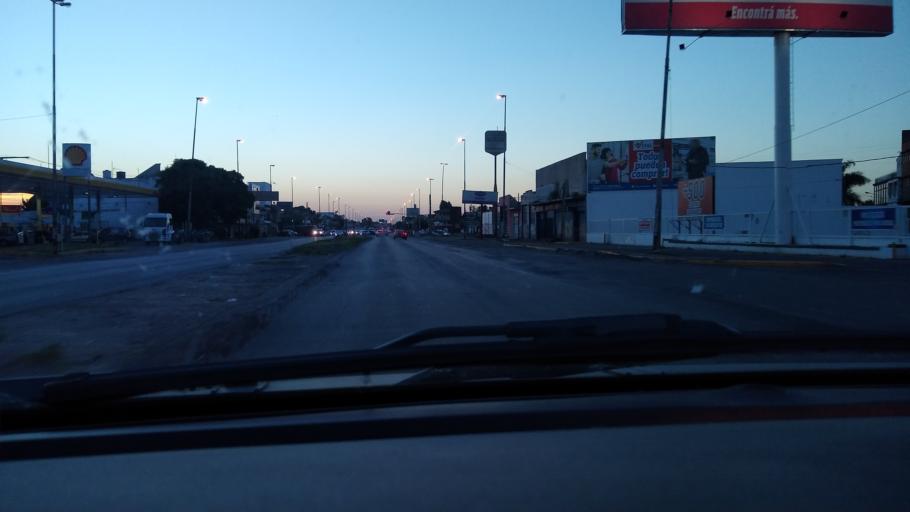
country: AR
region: Buenos Aires
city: San Justo
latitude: -34.6830
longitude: -58.5697
